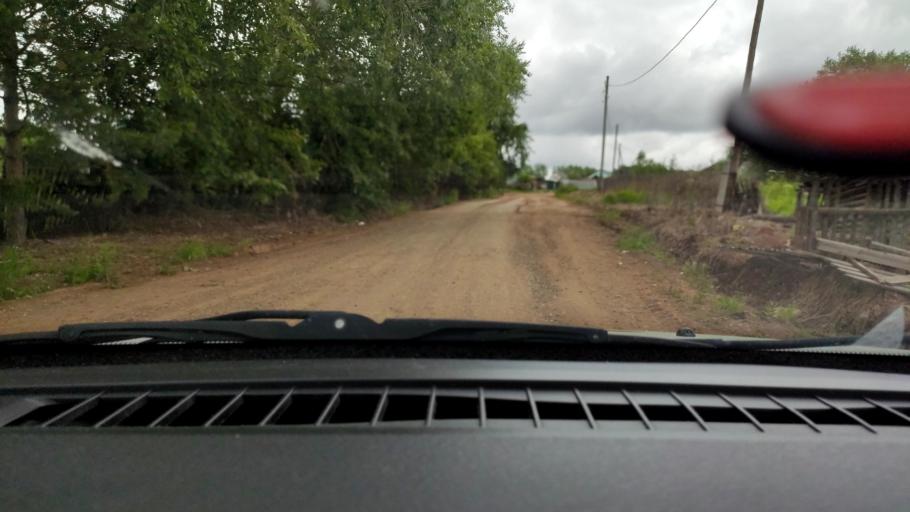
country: RU
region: Perm
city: Chaykovskaya
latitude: 58.1437
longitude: 55.5672
